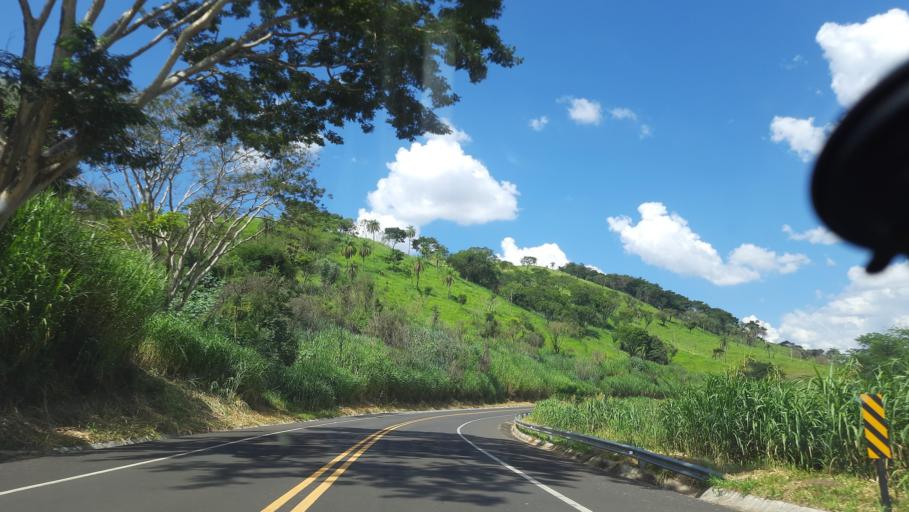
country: BR
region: Sao Paulo
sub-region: Sao Jose Do Rio Pardo
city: Sao Jose do Rio Pardo
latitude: -21.6049
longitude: -46.9700
